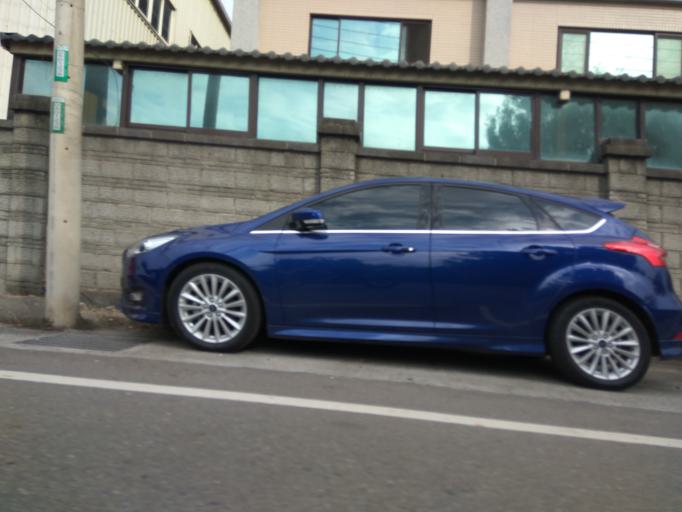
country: TW
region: Taiwan
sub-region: Hsinchu
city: Zhubei
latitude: 24.9858
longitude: 121.0317
